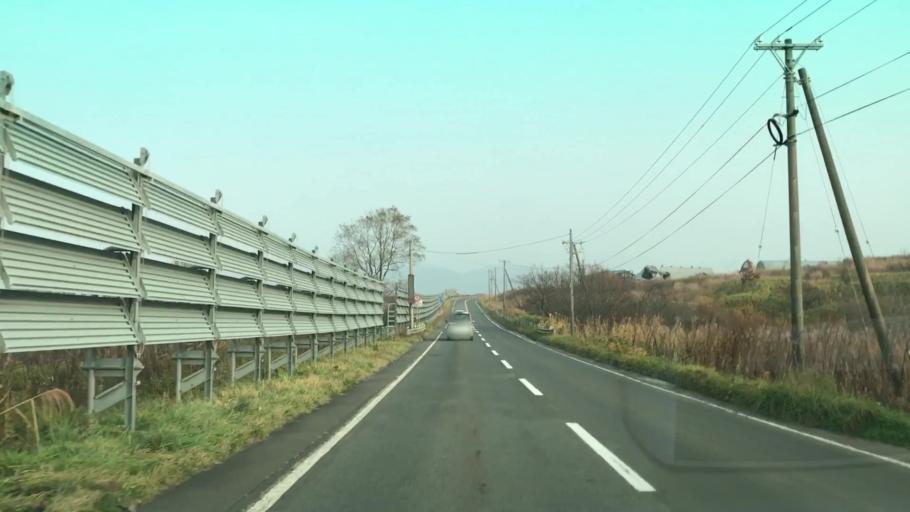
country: JP
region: Hokkaido
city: Ishikari
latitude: 43.3466
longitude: 141.4243
